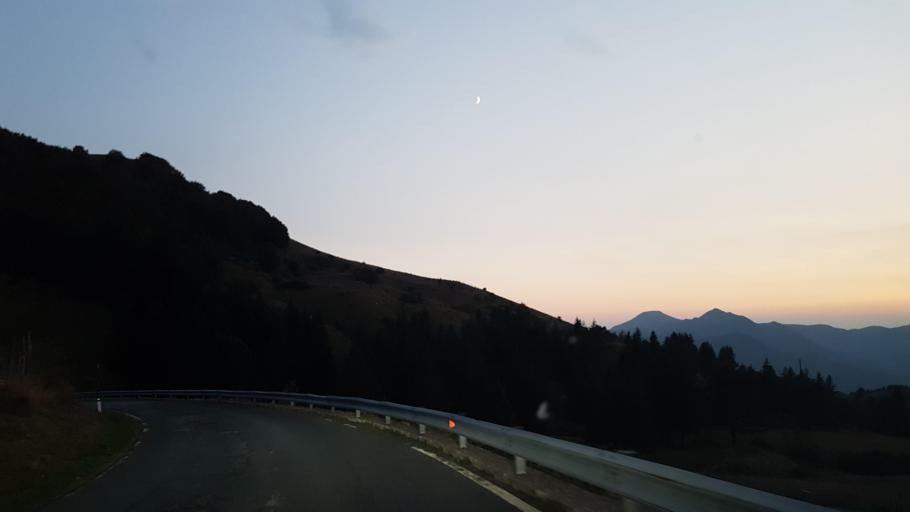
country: IT
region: Liguria
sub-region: Provincia di La Spezia
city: Varese Ligure
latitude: 44.4095
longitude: 9.6266
